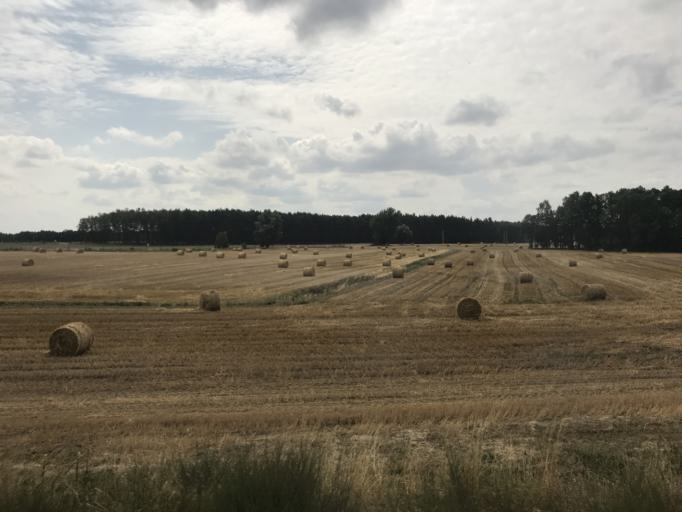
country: PL
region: Greater Poland Voivodeship
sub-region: Powiat gnieznienski
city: Trzemeszno
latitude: 52.5472
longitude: 17.7443
